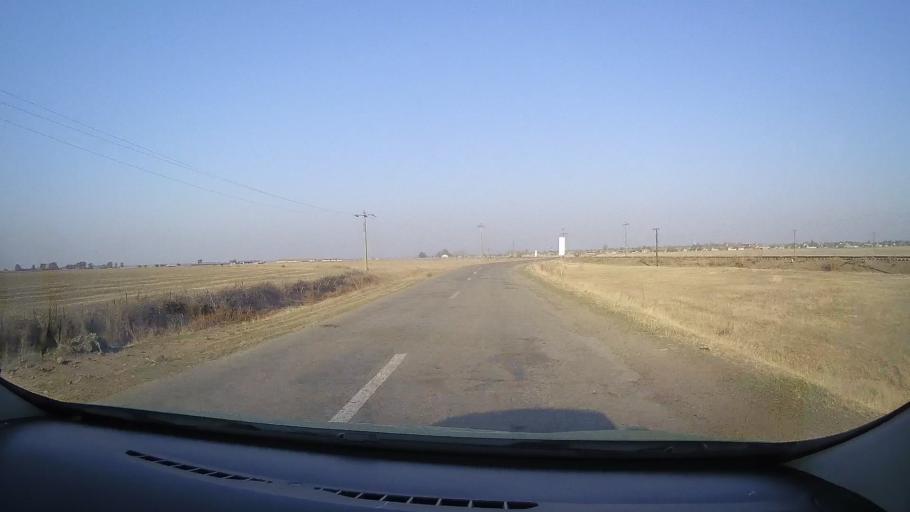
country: RO
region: Arad
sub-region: Comuna Graniceri
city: Graniceri
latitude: 46.5095
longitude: 21.3155
